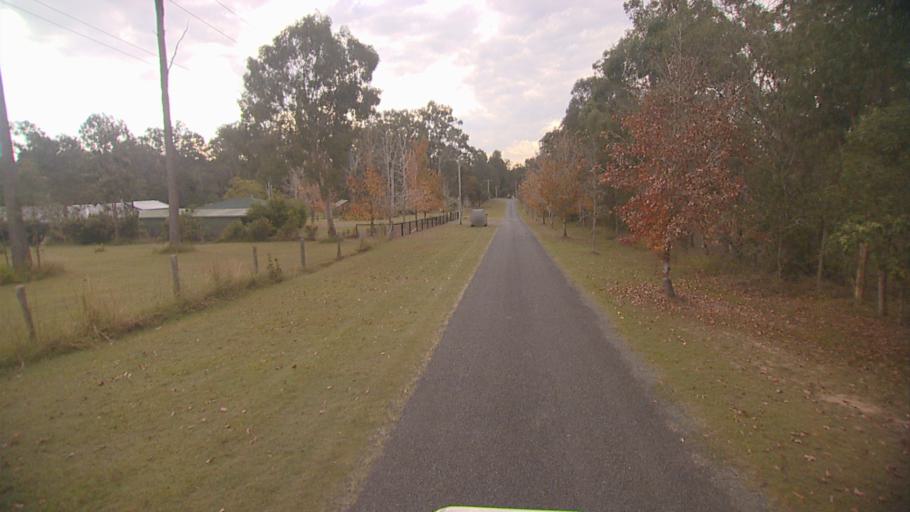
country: AU
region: Queensland
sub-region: Logan
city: Chambers Flat
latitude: -27.7829
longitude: 153.1125
